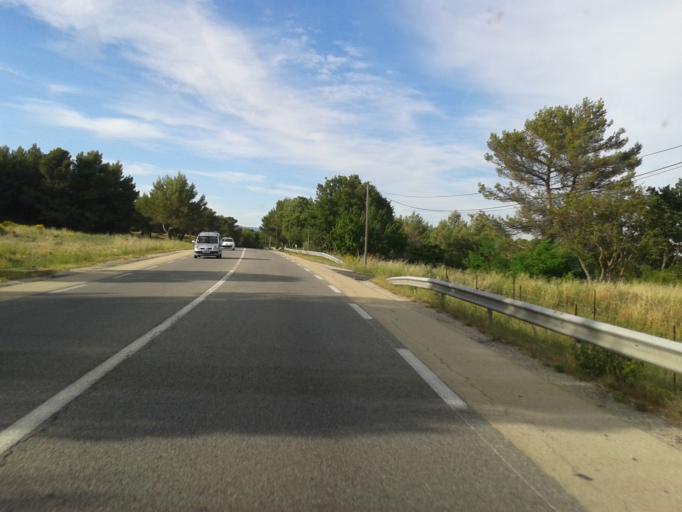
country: FR
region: Provence-Alpes-Cote d'Azur
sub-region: Departement des Bouches-du-Rhone
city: Venelles
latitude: 43.6176
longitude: 5.5055
